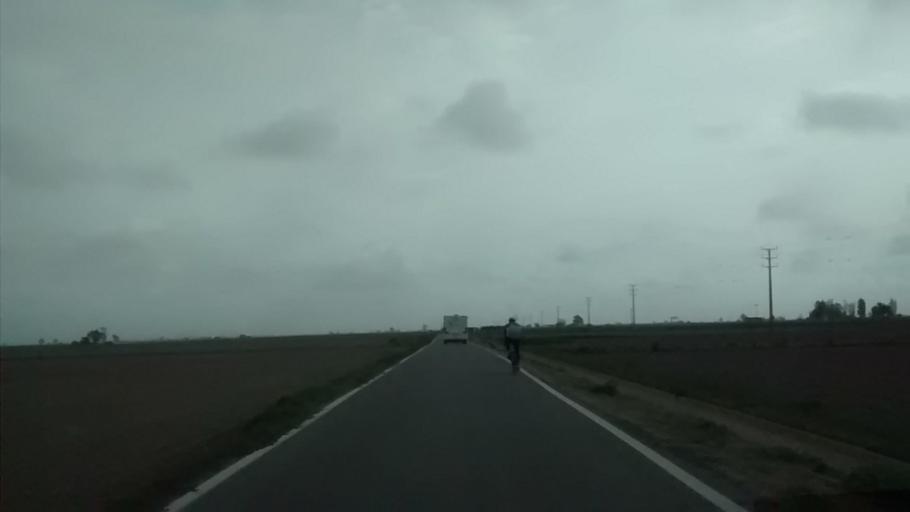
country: ES
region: Catalonia
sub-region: Provincia de Tarragona
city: Sant Carles de la Rapita
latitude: 40.6585
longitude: 0.6352
